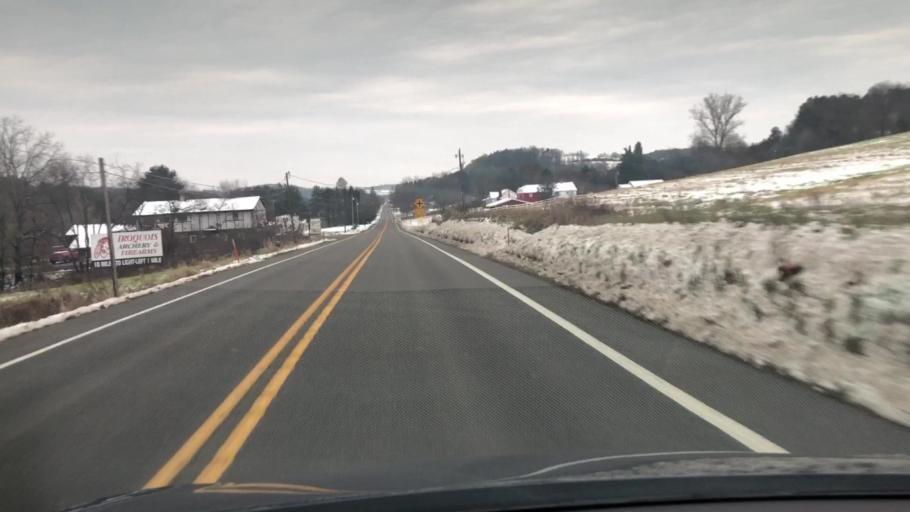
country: US
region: Pennsylvania
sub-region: Jefferson County
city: Brookville
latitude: 41.0768
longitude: -79.2351
